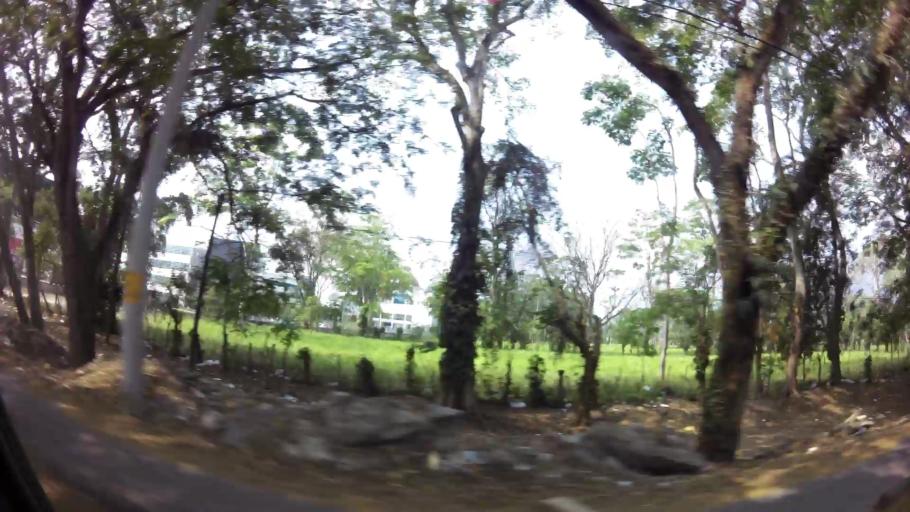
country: HN
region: Cortes
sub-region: San Pedro Sula
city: Pena Blanca
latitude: 15.5644
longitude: -88.0234
